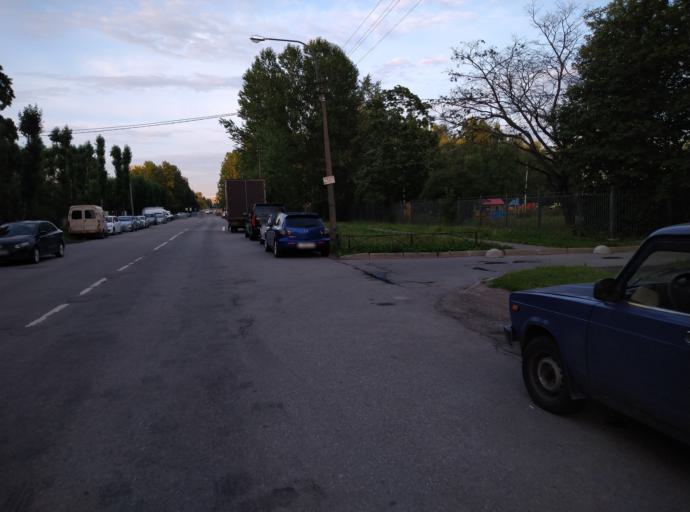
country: RU
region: St.-Petersburg
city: Kupchino
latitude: 59.8487
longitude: 30.3556
